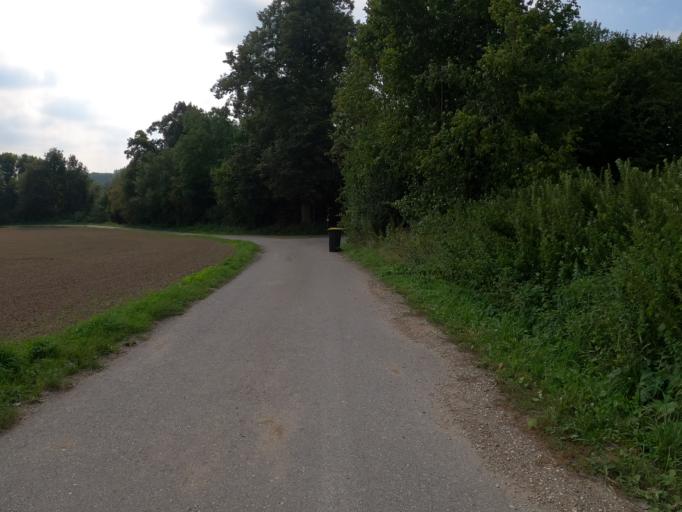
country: DE
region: Bavaria
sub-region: Swabia
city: Rettenbach
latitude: 48.4745
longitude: 10.3388
